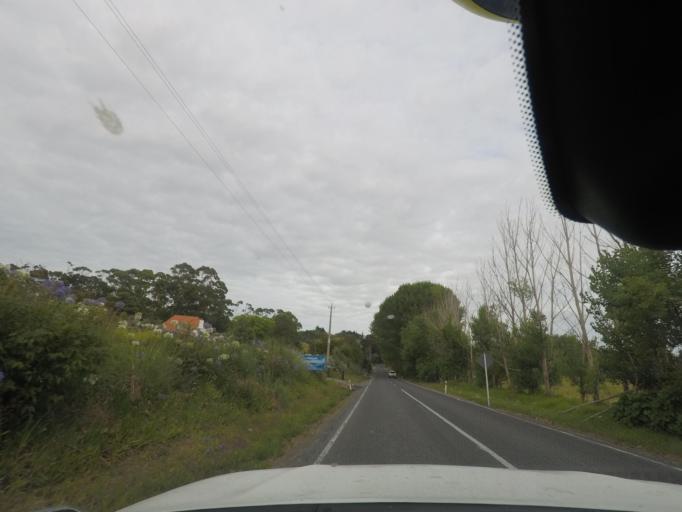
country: NZ
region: Auckland
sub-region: Auckland
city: Parakai
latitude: -36.5270
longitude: 174.2924
